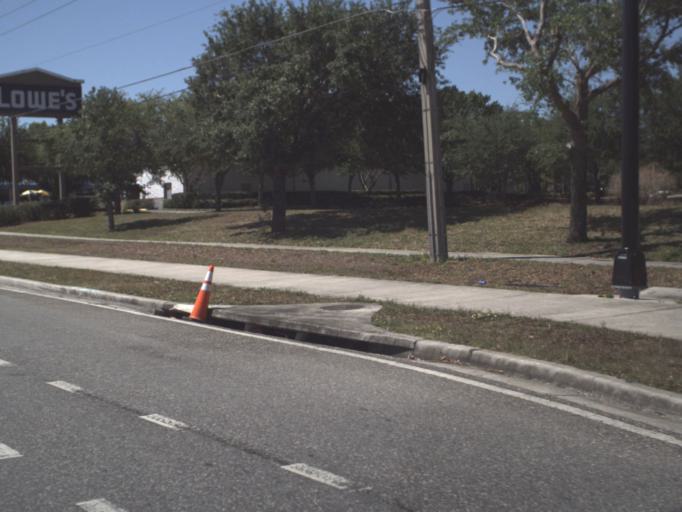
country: US
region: Florida
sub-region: Orange County
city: Conway
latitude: 28.5074
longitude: -81.3104
